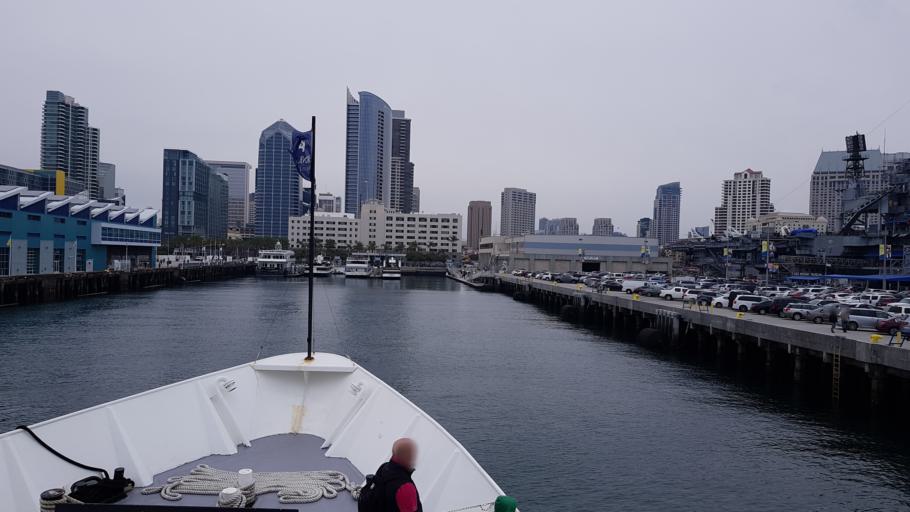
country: US
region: California
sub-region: San Diego County
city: San Diego
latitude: 32.7151
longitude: -117.1768
